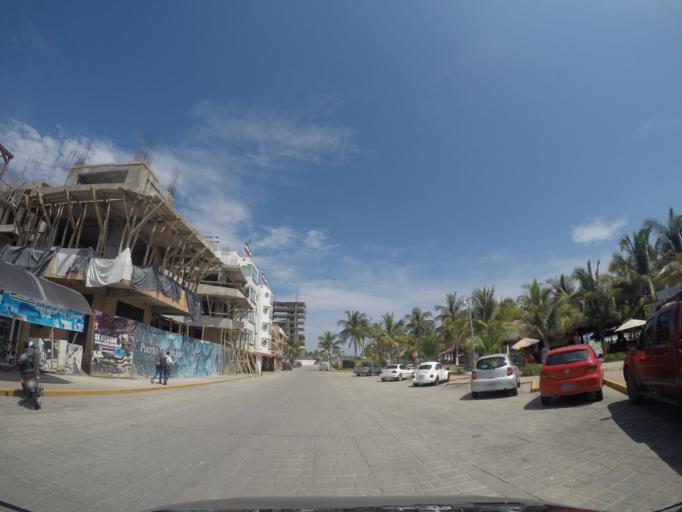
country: MX
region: Oaxaca
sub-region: Santa Maria Colotepec
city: Brisas de Zicatela
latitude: 15.8517
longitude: -97.0550
